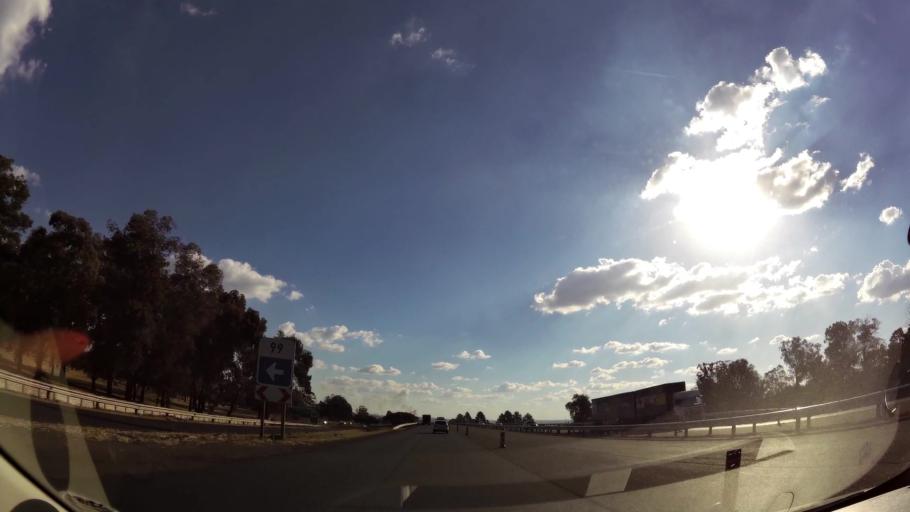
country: ZA
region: Mpumalanga
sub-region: Nkangala District Municipality
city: Witbank
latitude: -25.8849
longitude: 29.2099
